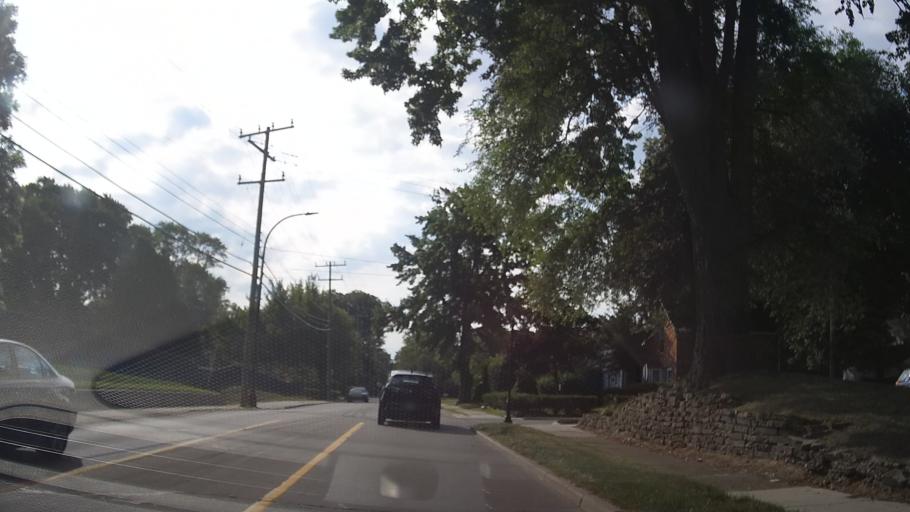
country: US
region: Michigan
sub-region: Wayne County
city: Grosse Pointe Farms
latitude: 42.4114
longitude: -82.8968
